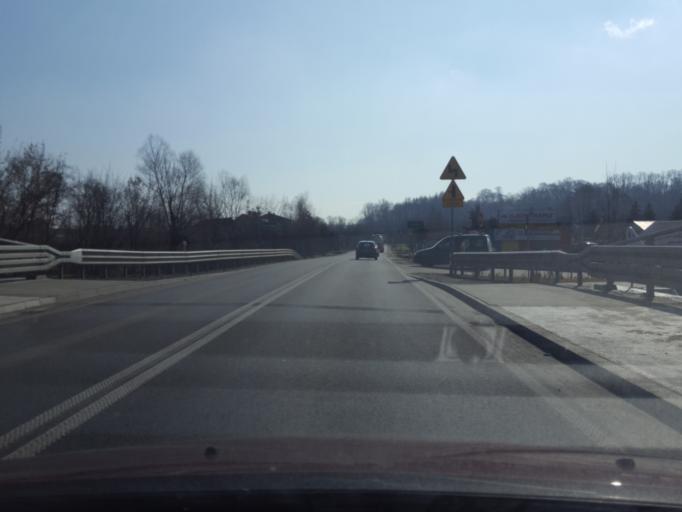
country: PL
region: Lesser Poland Voivodeship
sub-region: Powiat brzeski
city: Czchow
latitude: 49.8518
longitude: 20.6739
